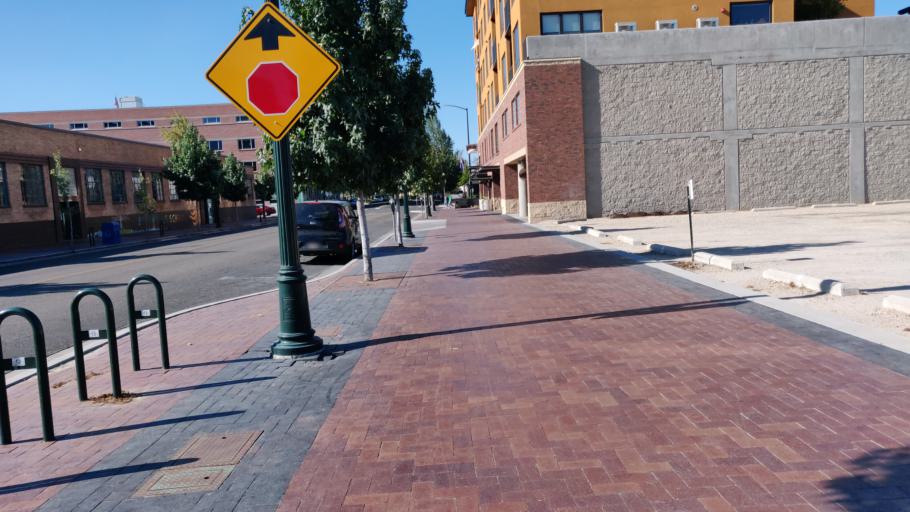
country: US
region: Idaho
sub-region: Ada County
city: Boise
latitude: 43.6118
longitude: -116.2073
